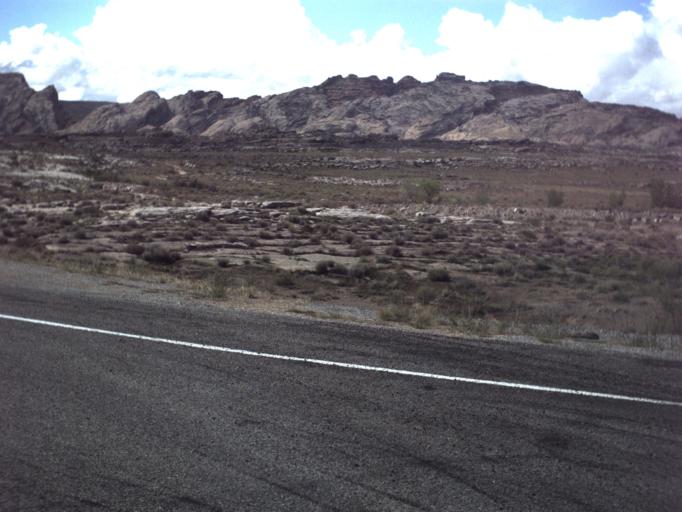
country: US
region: Utah
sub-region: Carbon County
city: East Carbon City
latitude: 38.9246
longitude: -110.3772
